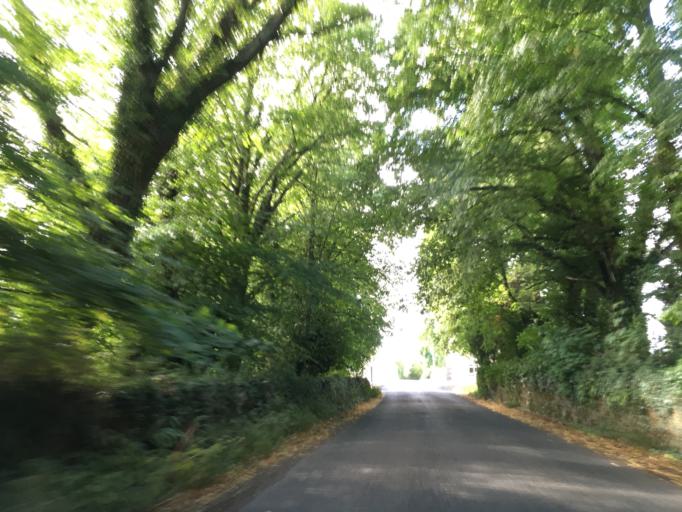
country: IE
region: Munster
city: Cahir
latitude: 52.2840
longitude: -7.9539
